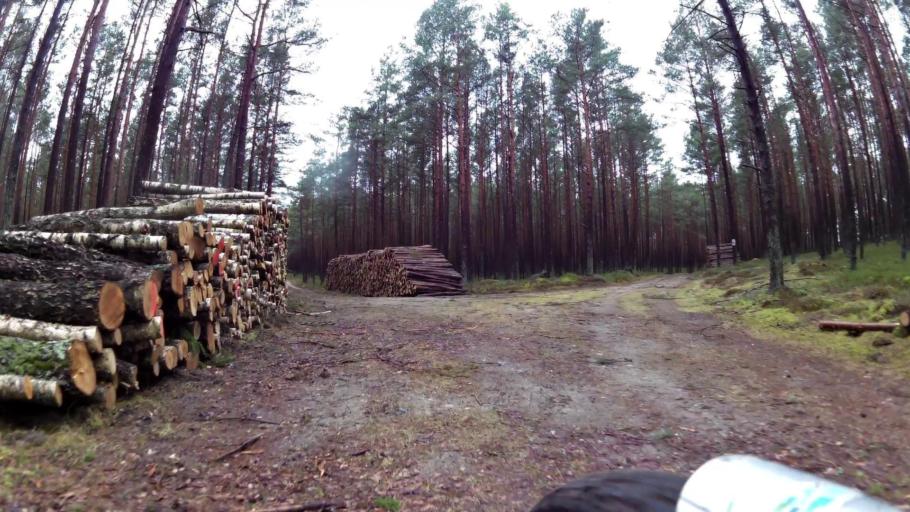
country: PL
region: Pomeranian Voivodeship
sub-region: Powiat bytowski
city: Borzytuchom
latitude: 54.2683
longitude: 17.4073
